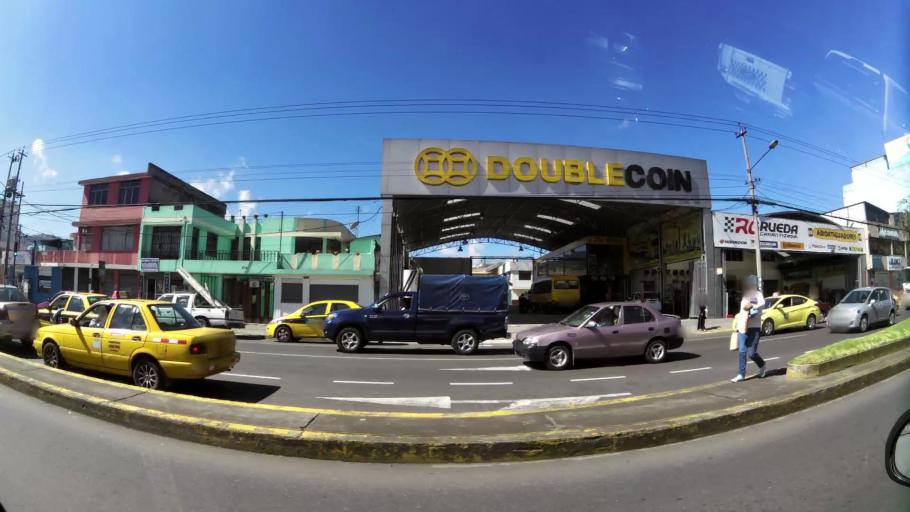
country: EC
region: Pichincha
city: Quito
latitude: -0.2492
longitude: -78.5300
